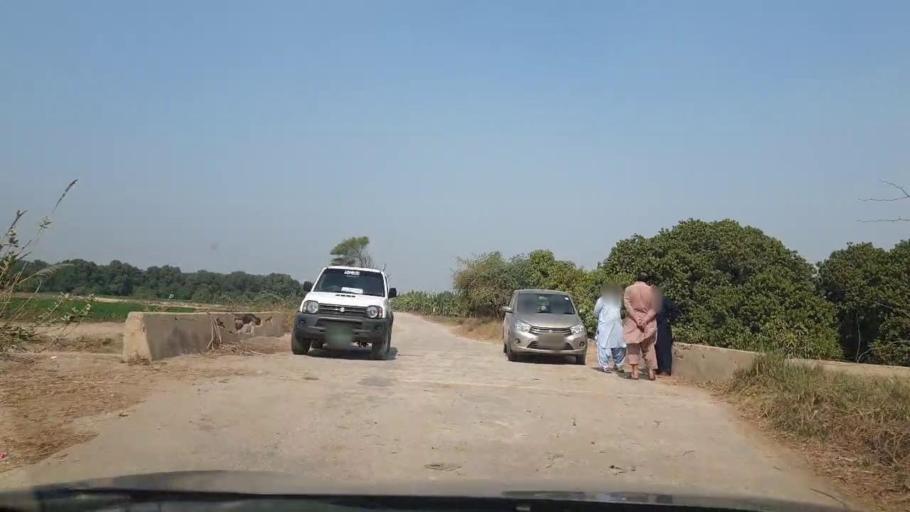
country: PK
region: Sindh
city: Tando Allahyar
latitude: 25.4826
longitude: 68.7918
